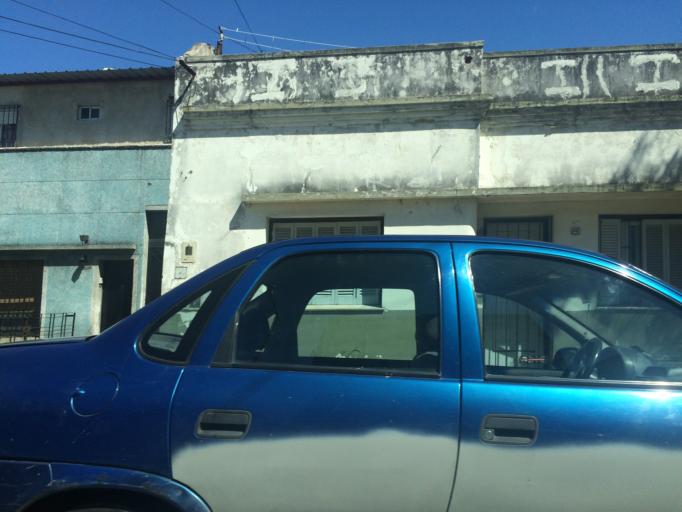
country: AR
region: Buenos Aires
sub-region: Partido de Lanus
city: Lanus
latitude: -34.7146
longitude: -58.3976
